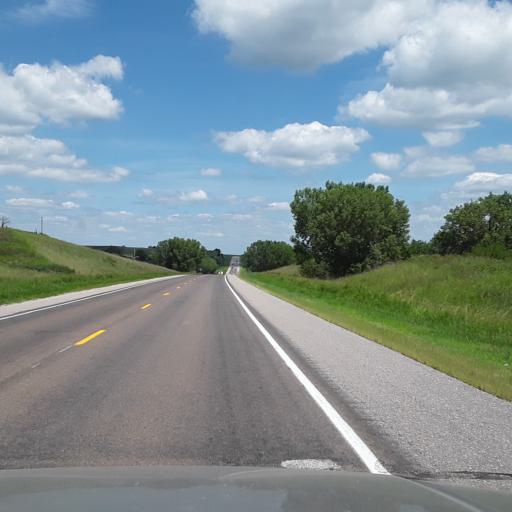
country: US
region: Nebraska
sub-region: Nance County
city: Genoa
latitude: 41.4691
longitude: -97.7144
